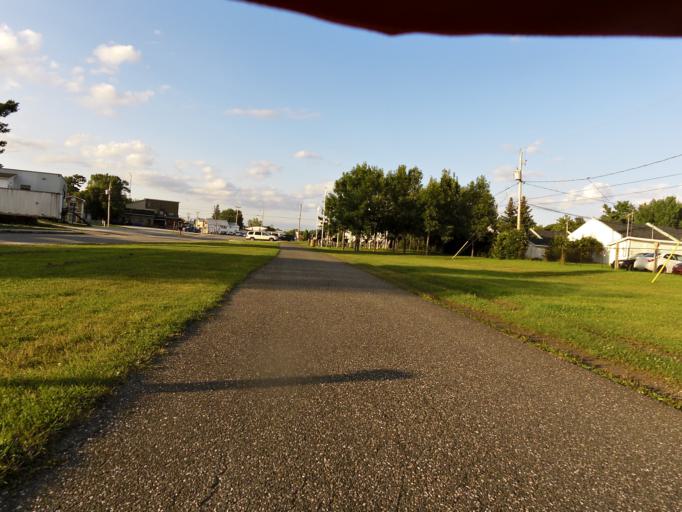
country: CA
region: Quebec
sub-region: Outaouais
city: Maniwaki
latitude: 46.3730
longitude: -75.9772
